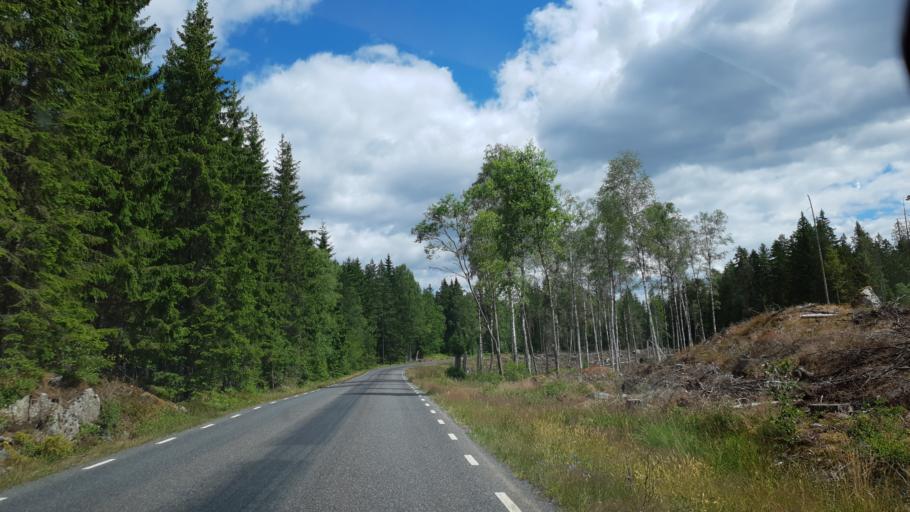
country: SE
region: Kronoberg
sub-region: Uppvidinge Kommun
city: Aseda
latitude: 57.1774
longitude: 15.3743
